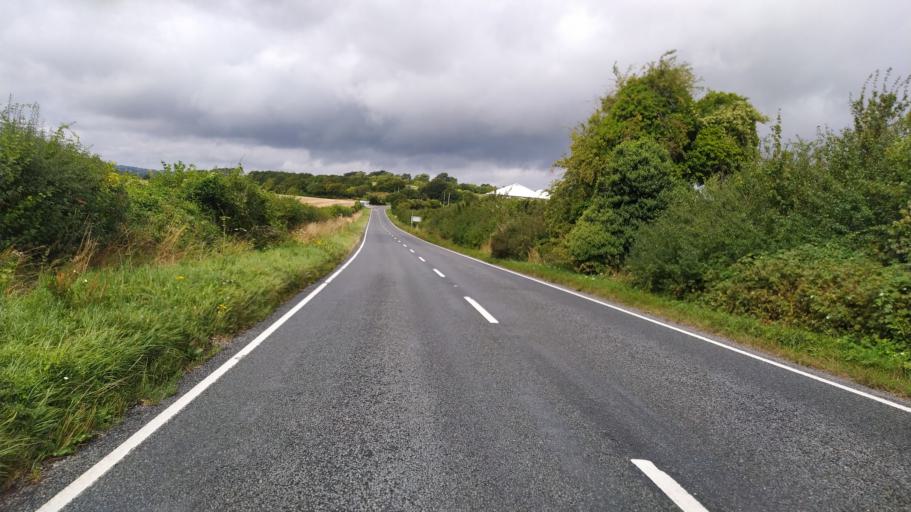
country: GB
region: England
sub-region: Hampshire
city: Kings Worthy
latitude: 51.0554
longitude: -1.2577
